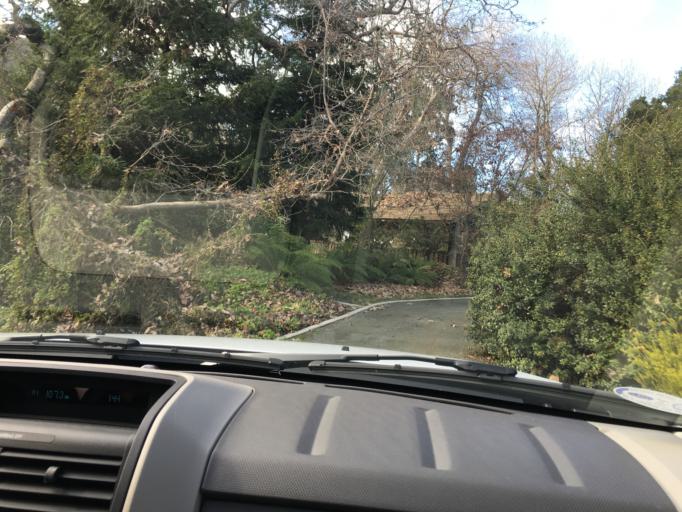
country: US
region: California
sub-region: San Luis Obispo County
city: Los Osos
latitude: 35.2885
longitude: -120.8033
